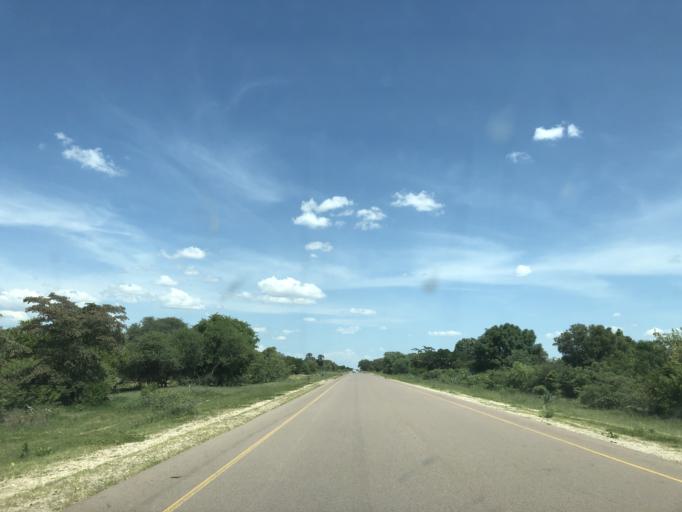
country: AO
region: Cunene
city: Ondjiva
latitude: -16.7959
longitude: 15.4211
